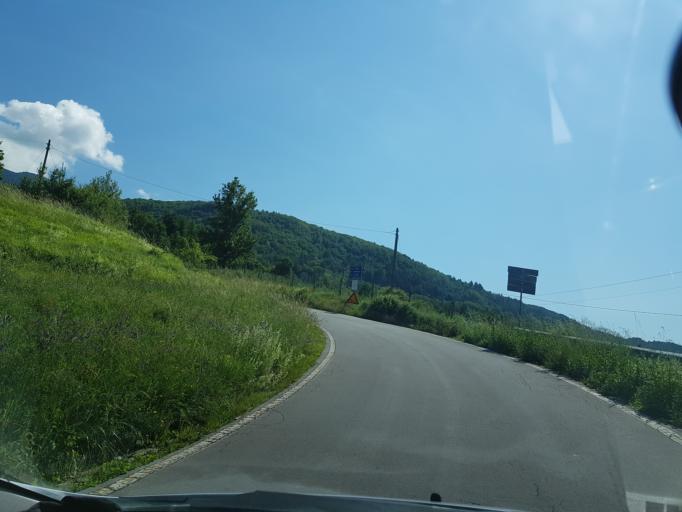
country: IT
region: Tuscany
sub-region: Provincia di Lucca
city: San Romano in Garfagnana
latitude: 44.1647
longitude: 10.3432
